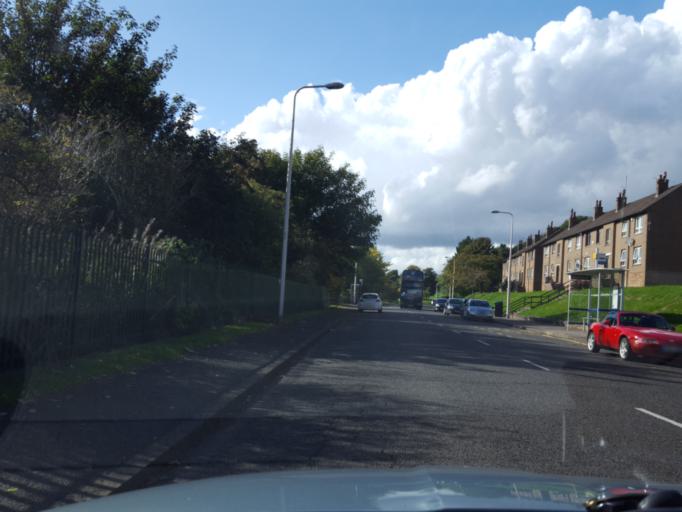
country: GB
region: Scotland
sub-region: Dundee City
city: Dundee
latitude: 56.4638
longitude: -3.0006
